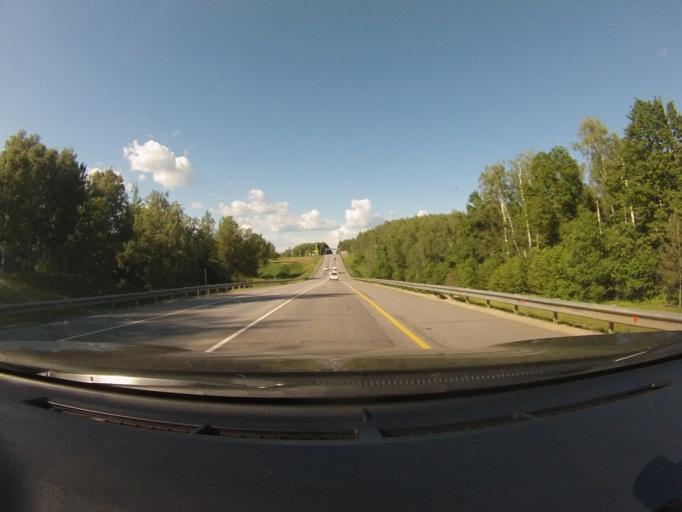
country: RU
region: Orjol
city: Spasskoye-Lutovinovo
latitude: 53.3477
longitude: 36.7123
